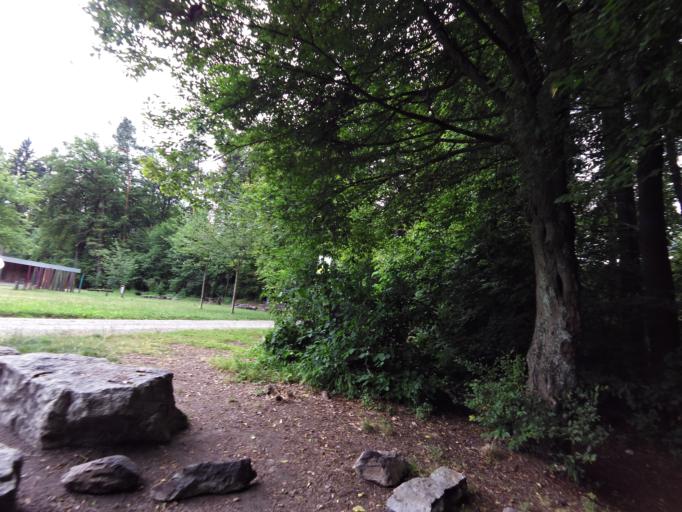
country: CH
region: Zurich
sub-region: Bezirk Zuerich
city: Zuerich (Kreis 5) / Escher-Wyss
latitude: 47.4034
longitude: 8.5151
